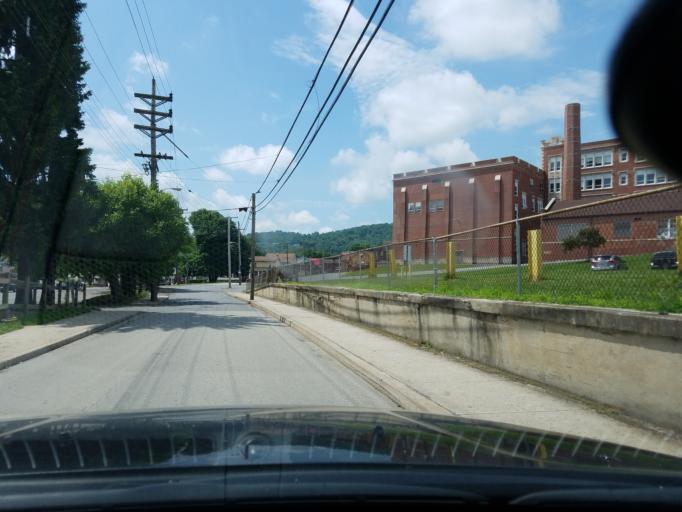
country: US
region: Pennsylvania
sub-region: Cambria County
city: Johnstown
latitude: 40.3514
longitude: -78.9439
